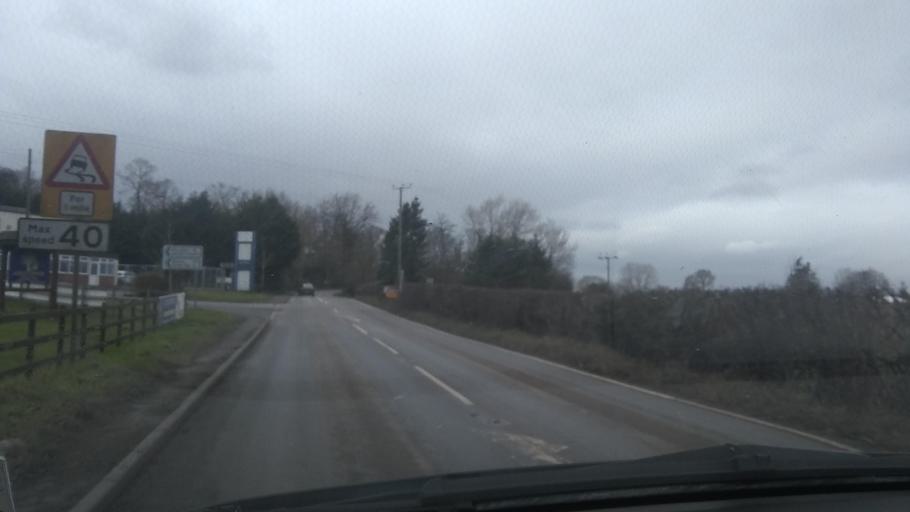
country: GB
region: England
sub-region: Shropshire
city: Cleobury Mortimer
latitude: 52.3783
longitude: -2.4457
